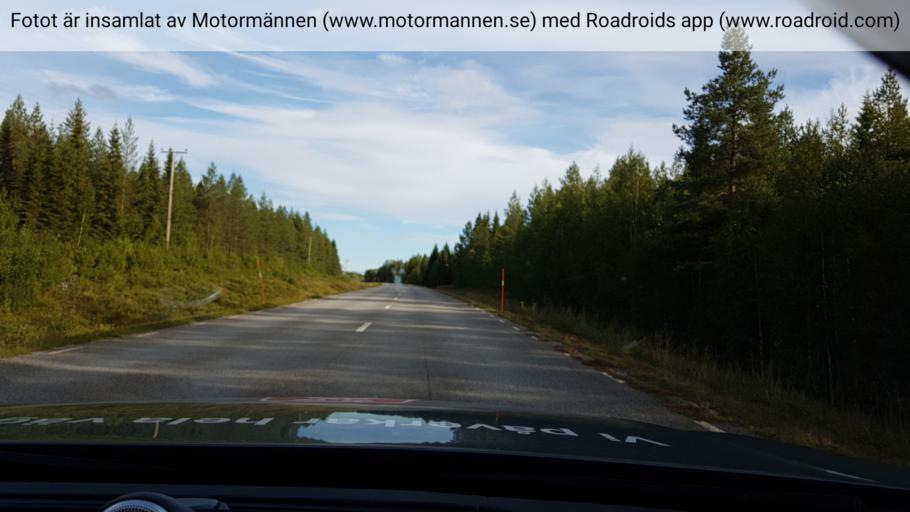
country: SE
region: Jaemtland
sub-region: Stroemsunds Kommun
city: Stroemsund
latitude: 64.2837
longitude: 15.3555
